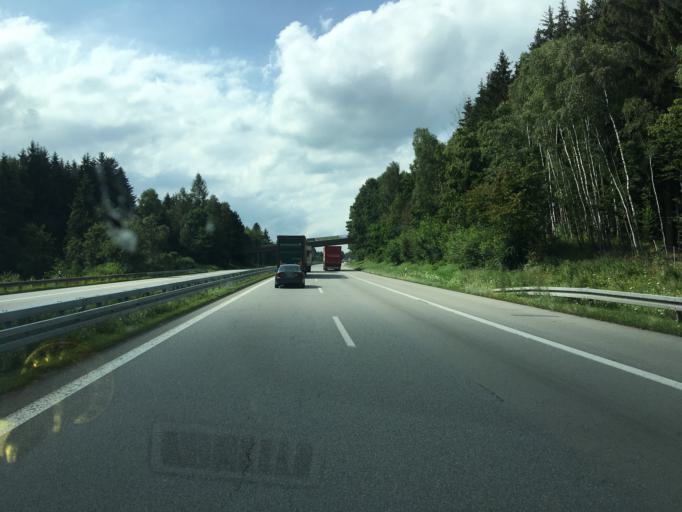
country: DE
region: Bavaria
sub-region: Lower Bavaria
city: Tiefenbach
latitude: 48.6123
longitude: 13.3614
